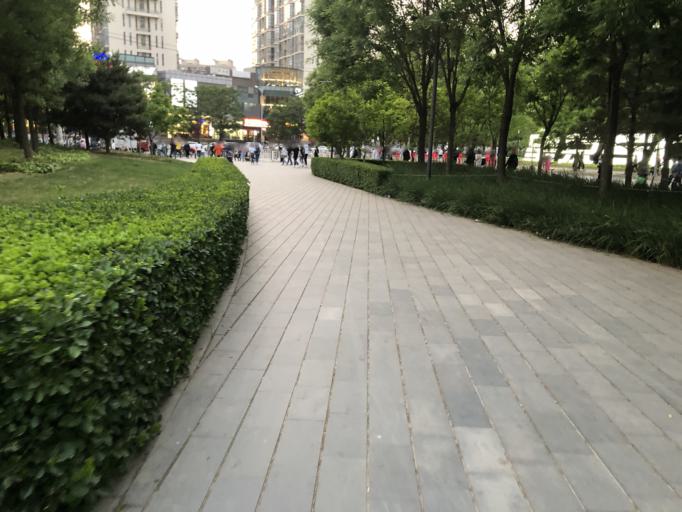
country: CN
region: Beijing
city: Wangjing
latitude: 39.9949
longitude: 116.4731
